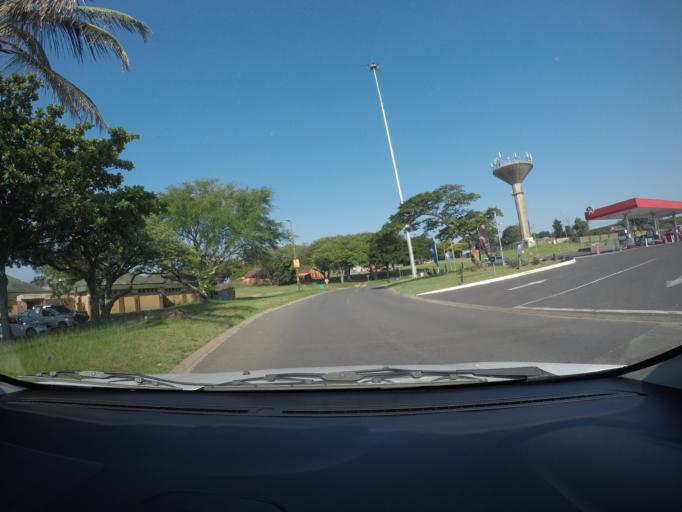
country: ZA
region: KwaZulu-Natal
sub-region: uThungulu District Municipality
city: Richards Bay
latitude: -28.7220
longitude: 32.0404
